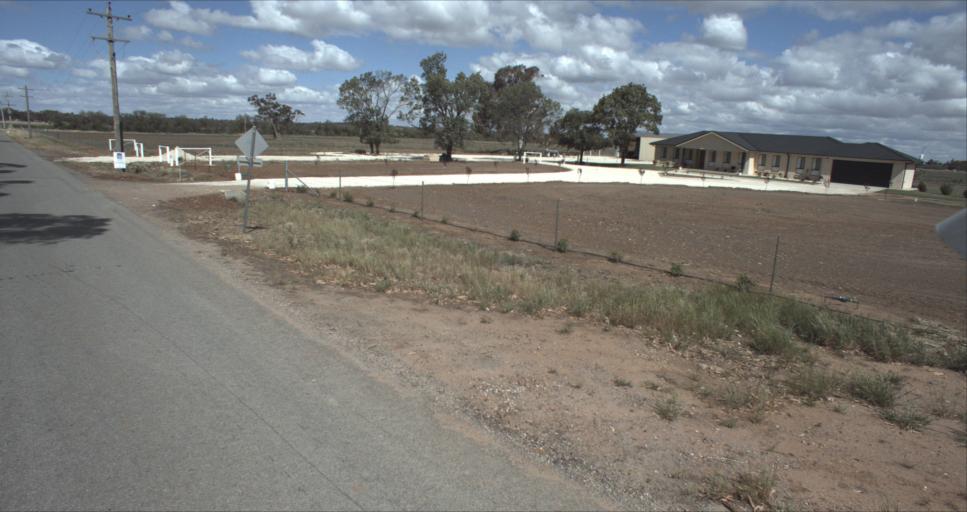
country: AU
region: New South Wales
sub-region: Leeton
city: Leeton
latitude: -34.5927
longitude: 146.4140
